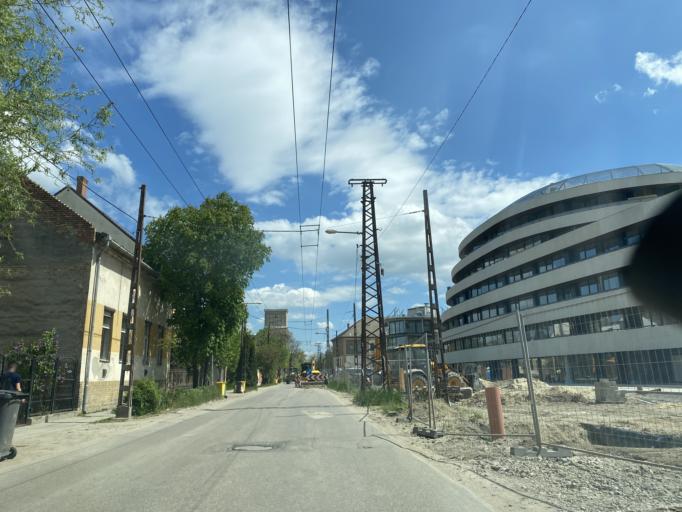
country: HU
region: Csongrad
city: Szeged
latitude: 46.2572
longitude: 20.1324
